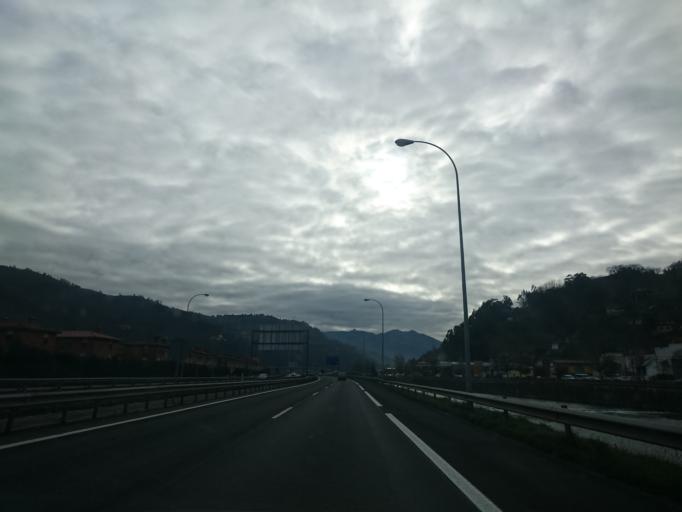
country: ES
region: Asturias
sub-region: Province of Asturias
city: Mieres
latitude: 43.2483
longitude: -5.7807
